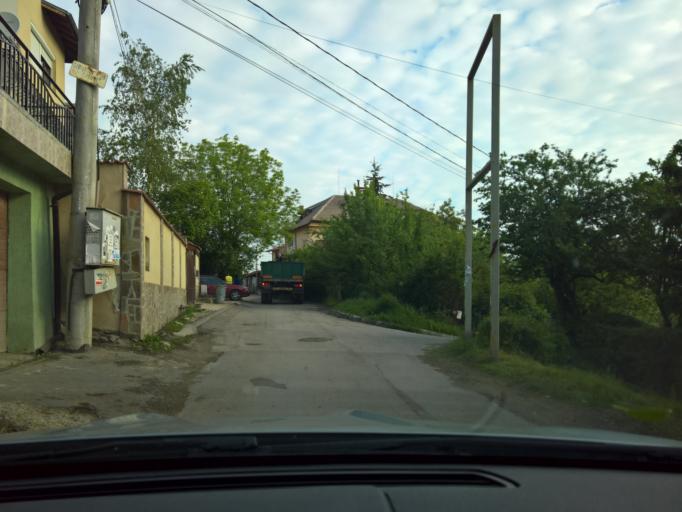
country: BG
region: Sofiya
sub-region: Obshtina Bozhurishte
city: Bozhurishte
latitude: 42.6804
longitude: 23.2326
